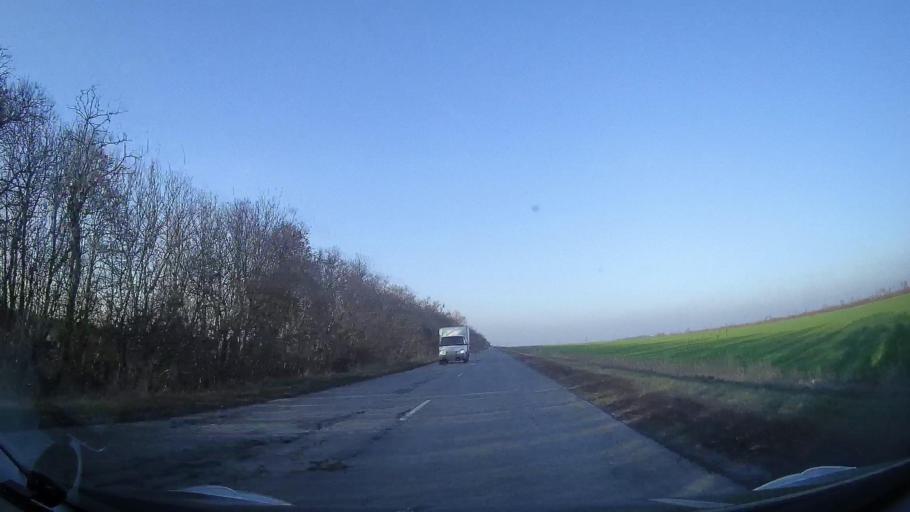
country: RU
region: Rostov
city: Kirovskaya
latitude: 47.0045
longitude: 39.9790
